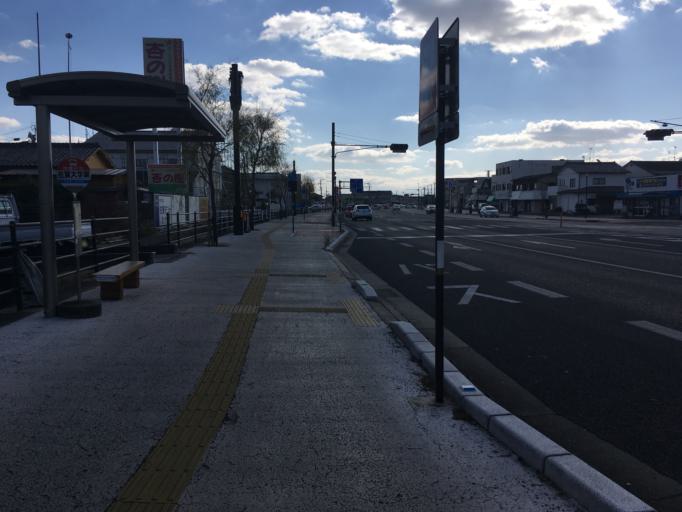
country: JP
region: Saga Prefecture
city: Saga-shi
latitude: 33.2417
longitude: 130.2943
